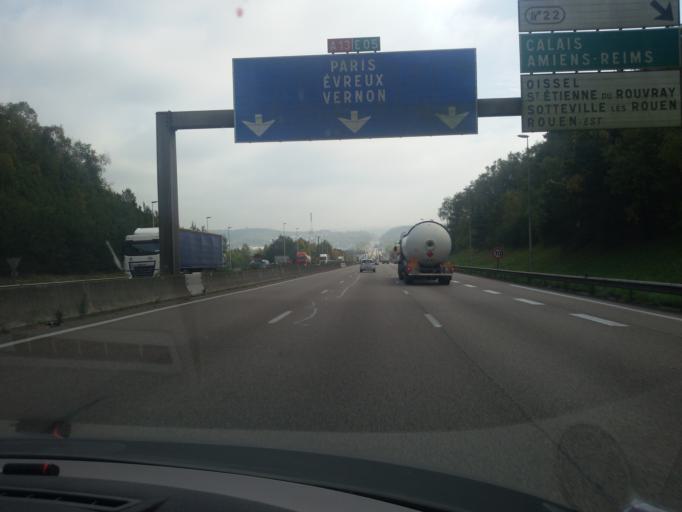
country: FR
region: Haute-Normandie
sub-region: Departement de la Seine-Maritime
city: Oissel
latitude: 49.3400
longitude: 1.0685
